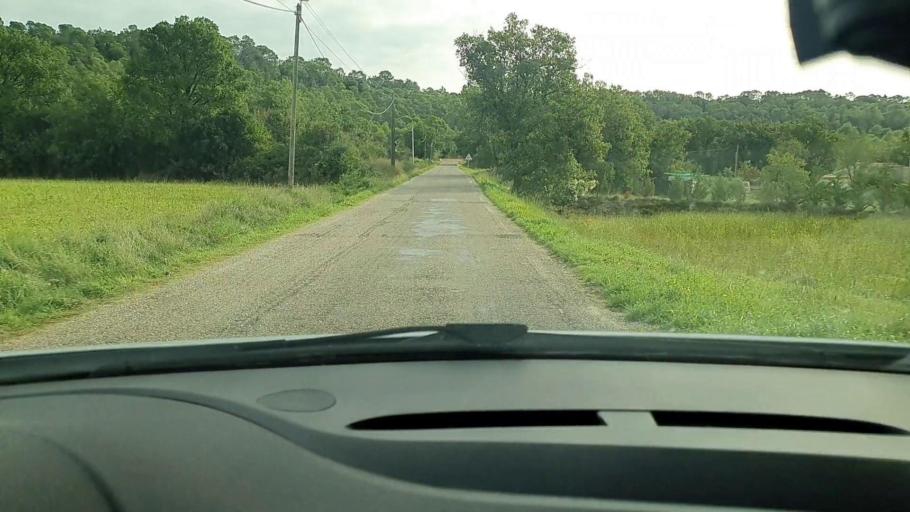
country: FR
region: Languedoc-Roussillon
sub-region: Departement du Gard
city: Montaren-et-Saint-Mediers
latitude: 44.0839
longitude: 4.3815
